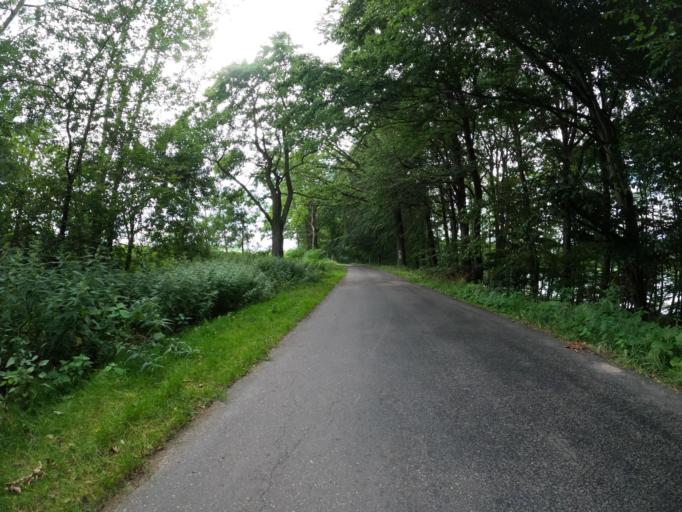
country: PL
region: West Pomeranian Voivodeship
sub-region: Powiat szczecinecki
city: Borne Sulinowo
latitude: 53.6330
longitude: 16.5432
